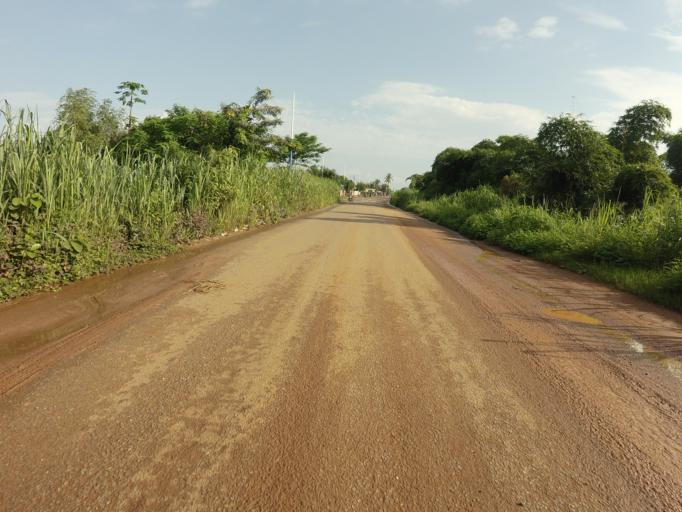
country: GH
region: Volta
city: Hohoe
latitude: 7.1180
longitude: 0.4574
